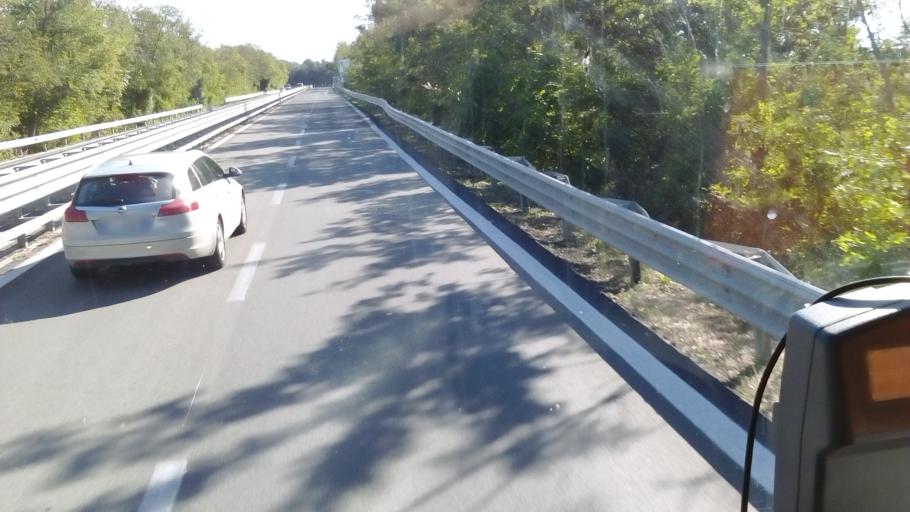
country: IT
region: Latium
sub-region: Provincia di Viterbo
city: Montalto di Castro
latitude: 42.3152
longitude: 11.6536
